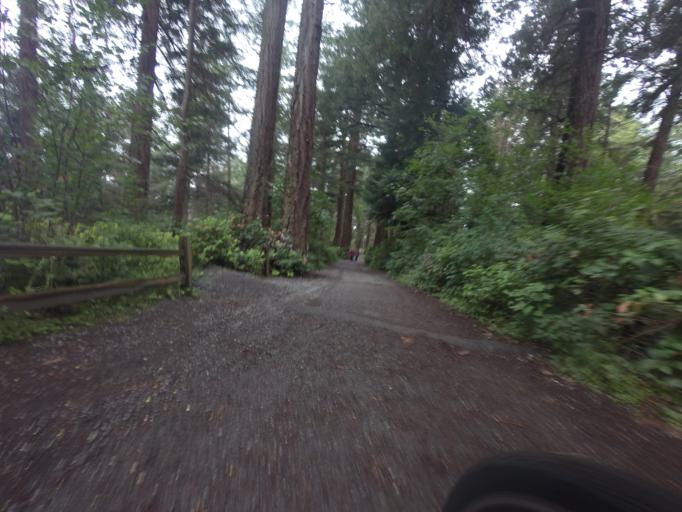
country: CA
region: British Columbia
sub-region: Greater Vancouver Regional District
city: Bowen Island
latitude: 49.3333
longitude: -123.2634
